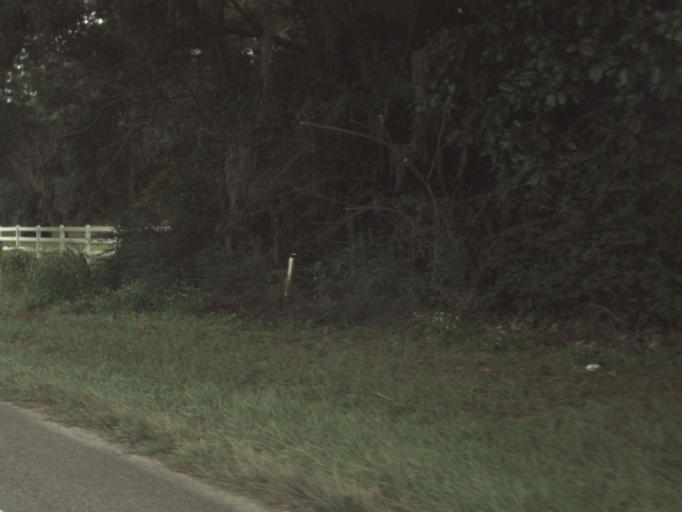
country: US
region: Florida
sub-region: Calhoun County
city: Blountstown
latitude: 30.4668
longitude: -85.0448
